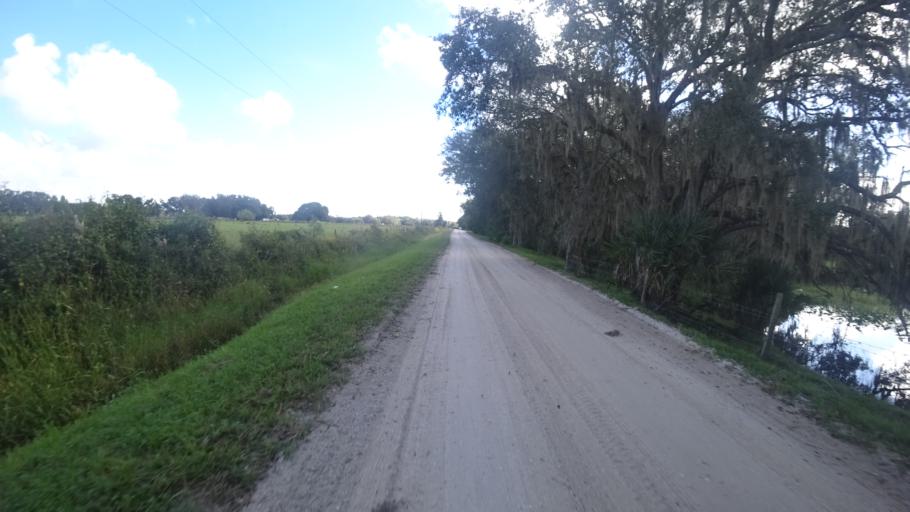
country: US
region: Florida
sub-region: Sarasota County
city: Lake Sarasota
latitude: 27.3069
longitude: -82.2258
